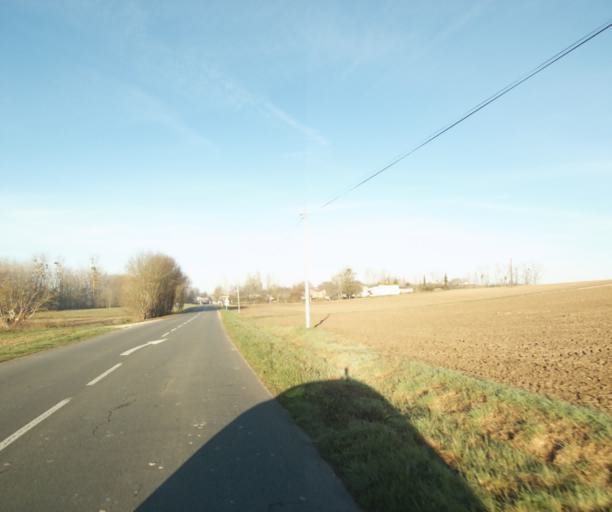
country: FR
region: Poitou-Charentes
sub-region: Departement de la Charente-Maritime
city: Cherac
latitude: 45.6965
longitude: -0.4814
